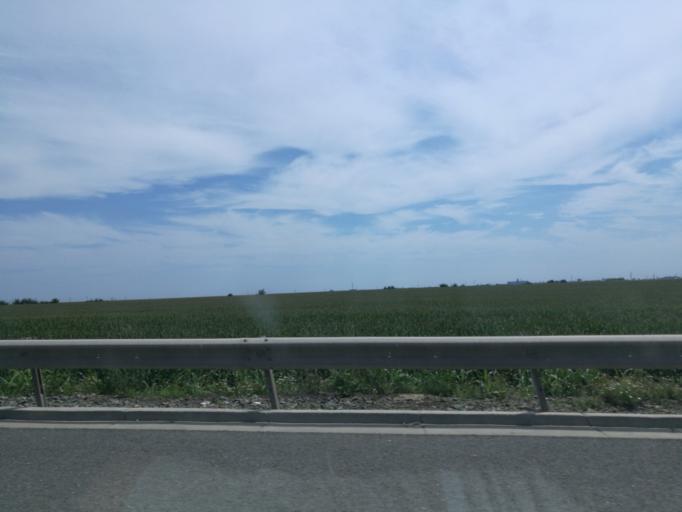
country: RO
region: Constanta
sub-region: Municipiul Constanta
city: Palazu Mare
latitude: 44.1890
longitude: 28.5511
